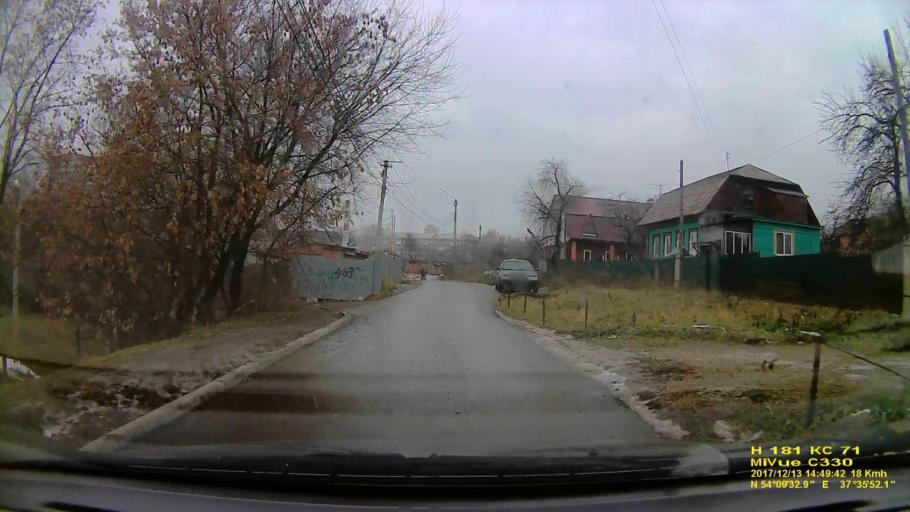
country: RU
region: Tula
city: Mendeleyevskiy
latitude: 54.1591
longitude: 37.5978
